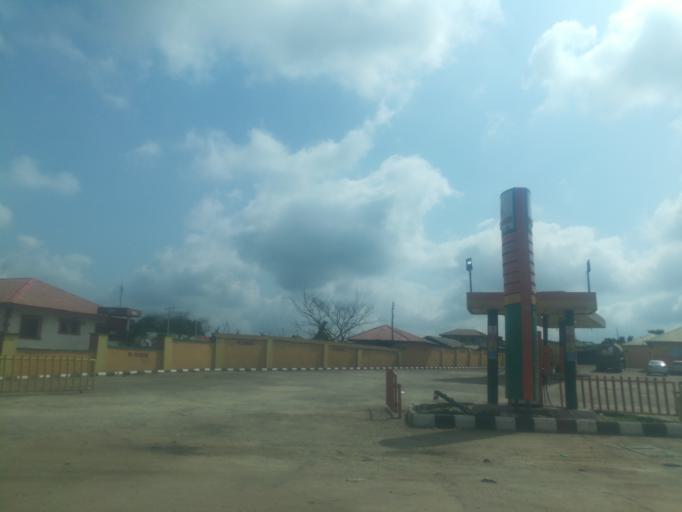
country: NG
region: Oyo
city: Moniya
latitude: 7.5352
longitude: 3.9165
